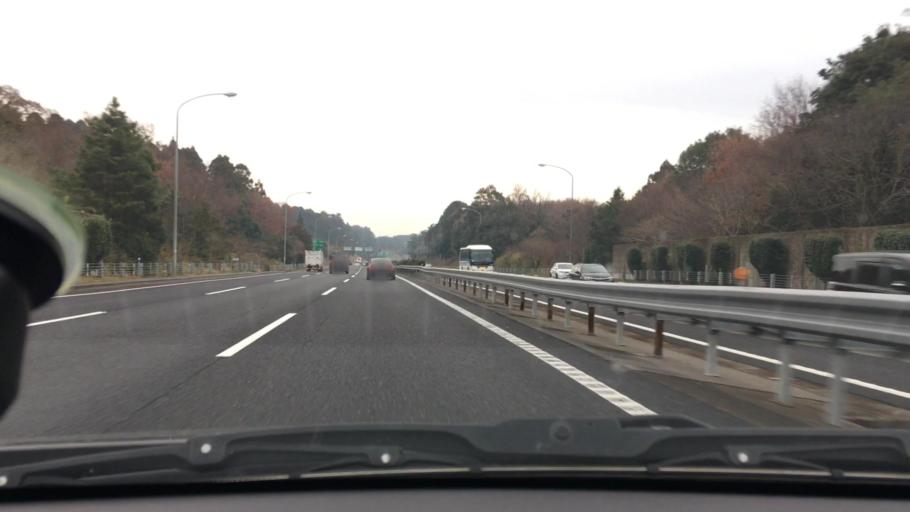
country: JP
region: Chiba
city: Narita
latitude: 35.7537
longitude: 140.3184
